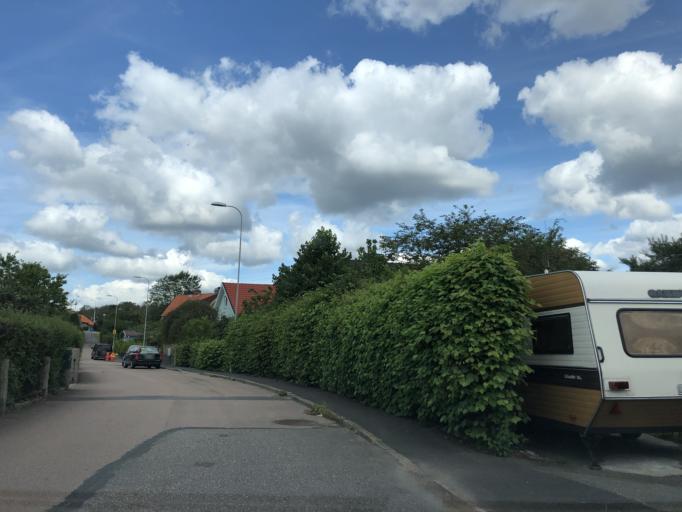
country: SE
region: Vaestra Goetaland
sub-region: Goteborg
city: Majorna
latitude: 57.7206
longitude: 11.9157
